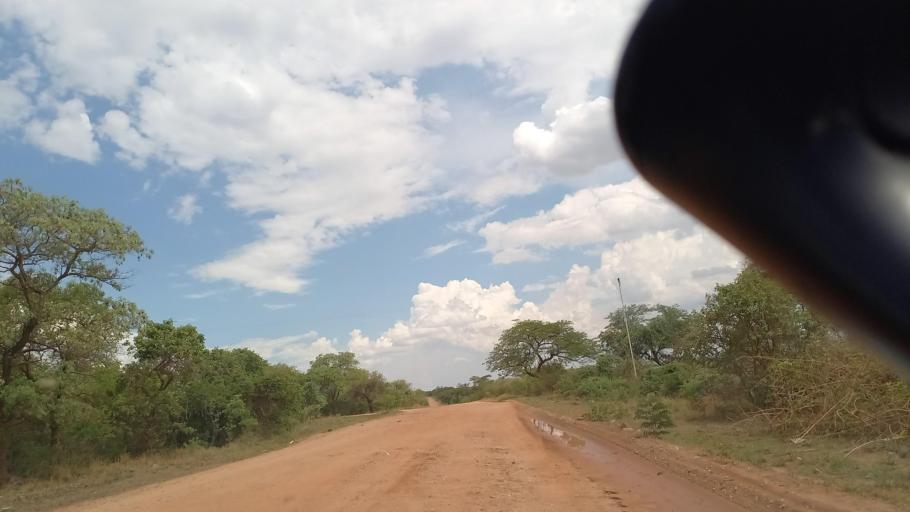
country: ZM
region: Southern
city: Nakambala
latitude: -16.0458
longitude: 27.9763
